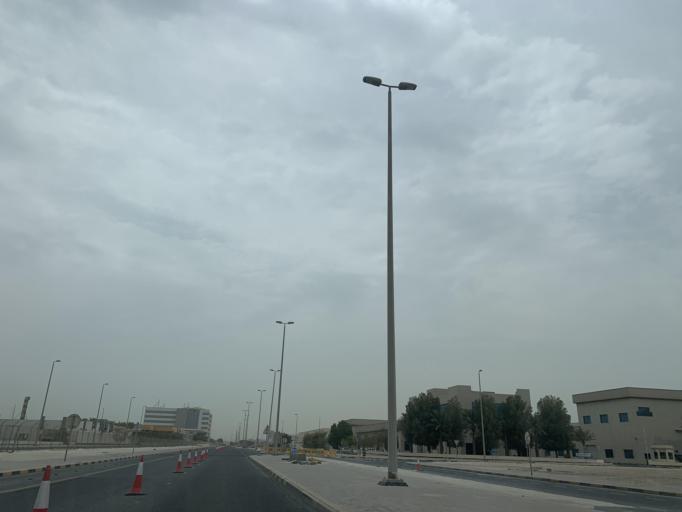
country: BH
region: Muharraq
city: Al Hadd
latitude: 26.2185
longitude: 50.6674
